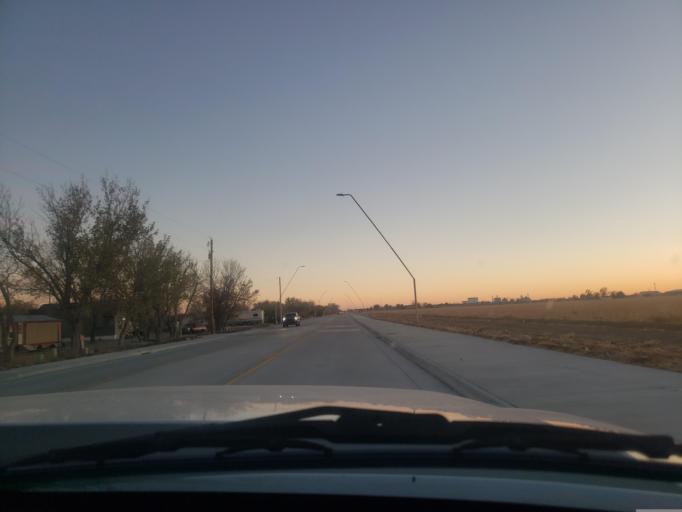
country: US
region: Kansas
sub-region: Finney County
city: Garden City
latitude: 37.9815
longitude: -100.8290
